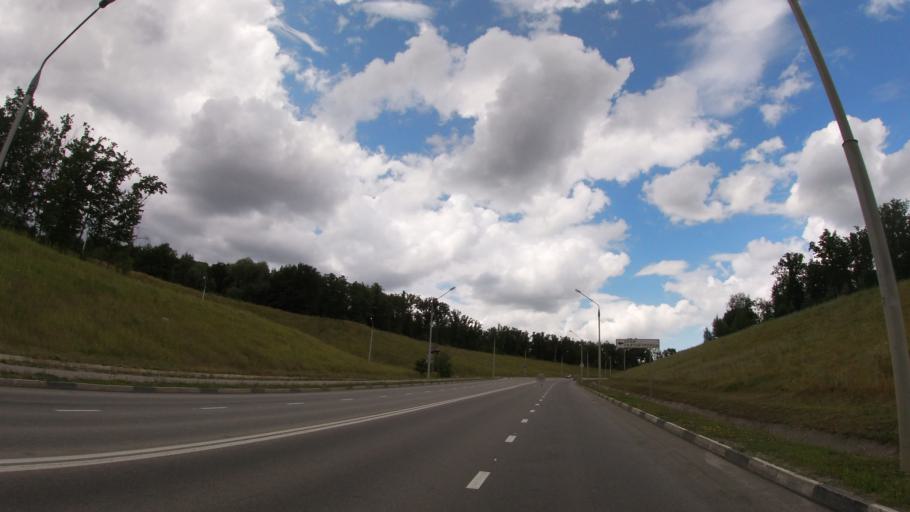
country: RU
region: Belgorod
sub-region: Belgorodskiy Rayon
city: Belgorod
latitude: 50.6222
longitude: 36.6135
